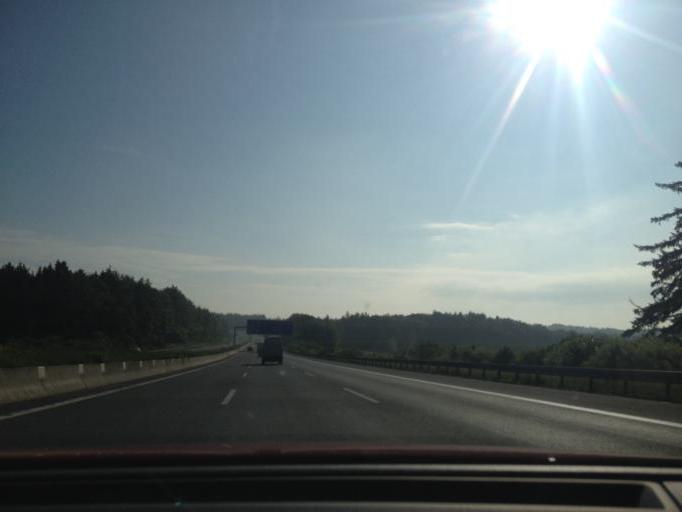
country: DE
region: Bavaria
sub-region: Regierungsbezirk Mittelfranken
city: Simmelsdorf
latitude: 49.6162
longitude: 11.3951
